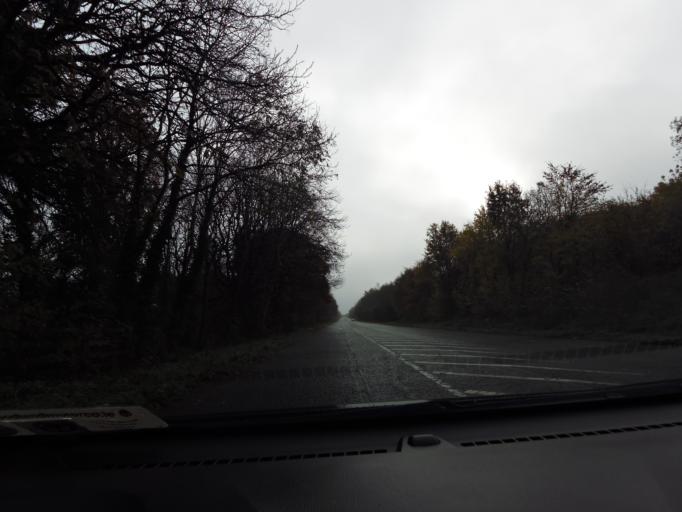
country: IE
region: Leinster
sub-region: An Iarmhi
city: Athlone
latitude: 53.3998
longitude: -7.8592
